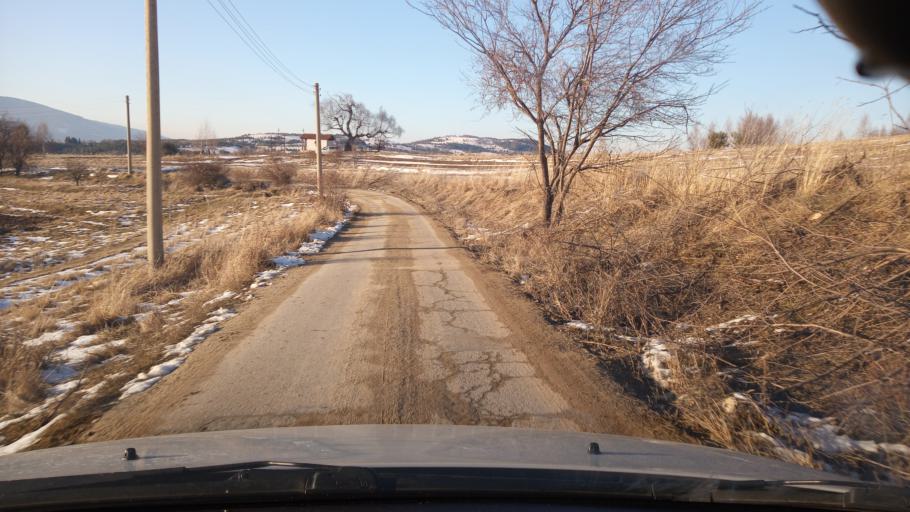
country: BG
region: Sofiya
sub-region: Obshtina Samokov
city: Samokov
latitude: 42.4801
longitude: 23.4178
